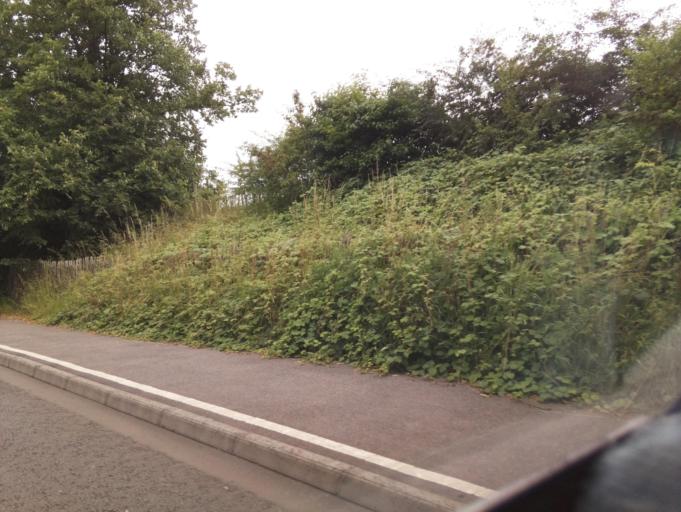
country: GB
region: England
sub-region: District of Rutland
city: Ryhall
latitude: 52.6655
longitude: -0.4675
